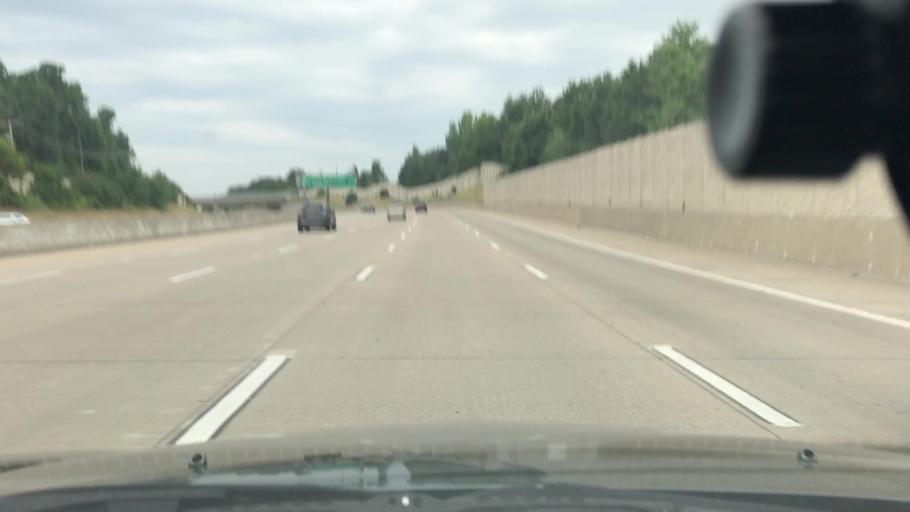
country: US
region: Missouri
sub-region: Saint Louis County
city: Maryland Heights
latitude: 38.7022
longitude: -90.4726
